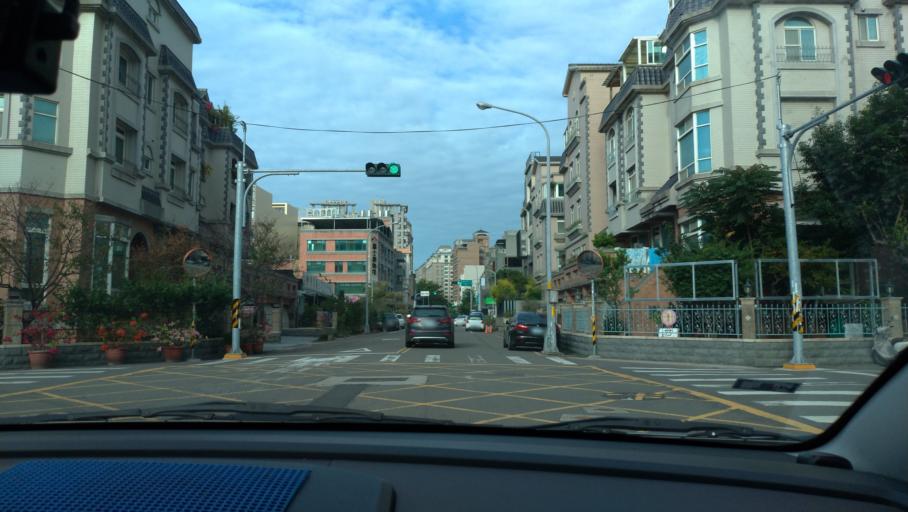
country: TW
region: Taiwan
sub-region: Hsinchu
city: Zhubei
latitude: 24.8169
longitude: 121.0239
